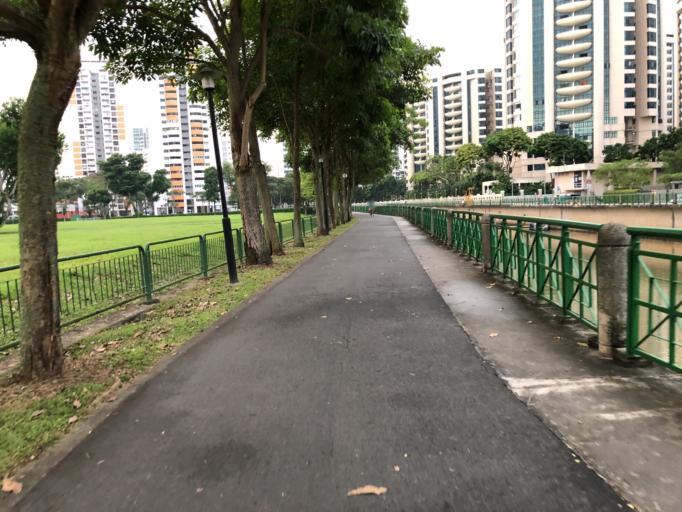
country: SG
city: Singapore
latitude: 1.2921
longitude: 103.8307
